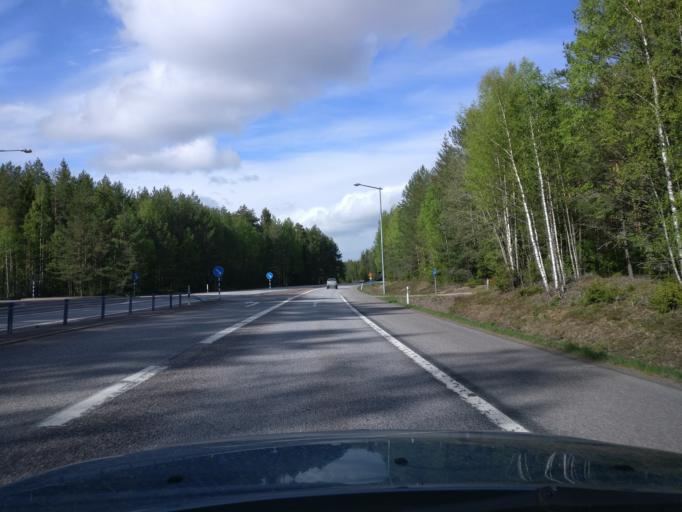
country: SE
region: Vaermland
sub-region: Forshaga Kommun
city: Forshaga
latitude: 59.4820
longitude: 13.4123
